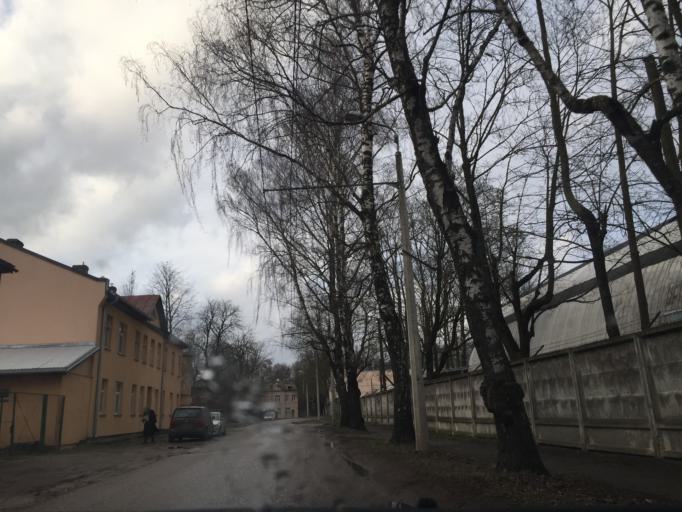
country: LV
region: Marupe
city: Marupe
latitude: 56.9372
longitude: 24.0532
